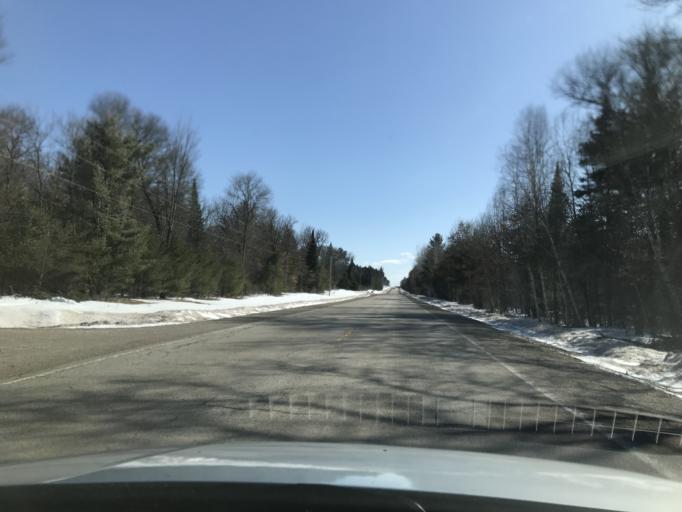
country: US
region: Wisconsin
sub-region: Marinette County
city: Niagara
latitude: 45.3669
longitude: -88.1005
